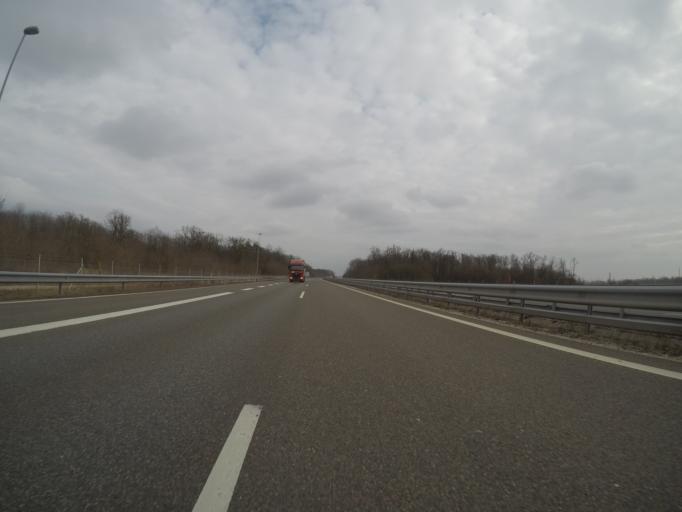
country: SI
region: Beltinci
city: Gancani
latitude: 46.6382
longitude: 16.2633
